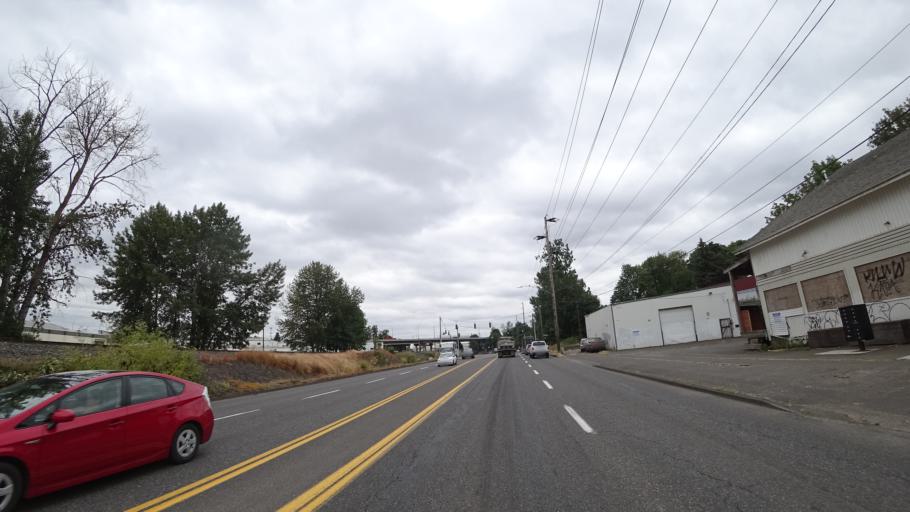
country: US
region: Washington
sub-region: Clark County
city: Vancouver
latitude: 45.5850
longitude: -122.6838
